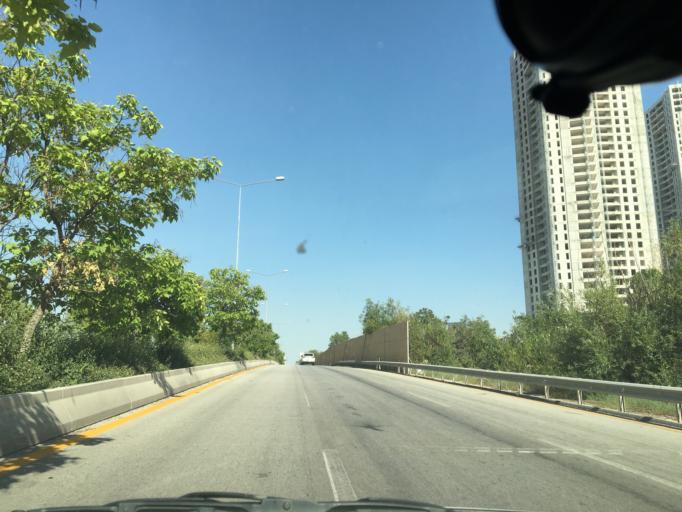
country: TR
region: Ankara
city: Ankara
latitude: 39.9179
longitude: 32.7892
